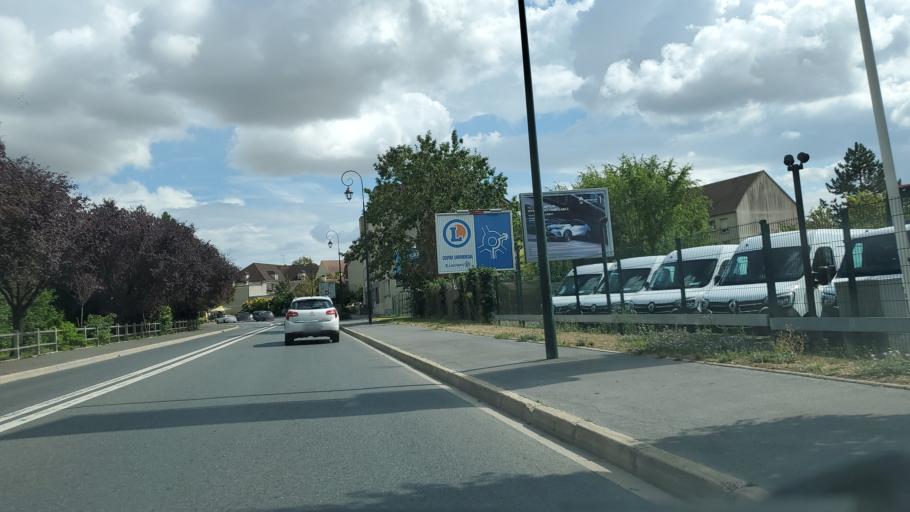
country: FR
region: Ile-de-France
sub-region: Departement de Seine-et-Marne
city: Coulommiers
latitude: 48.8095
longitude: 3.0809
